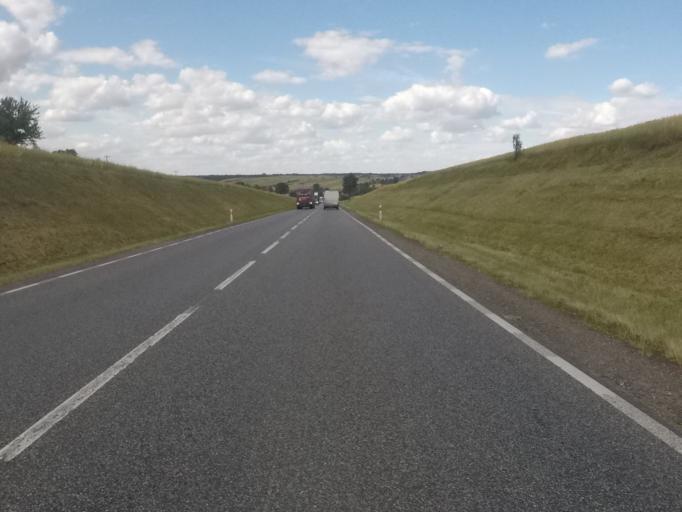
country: PL
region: Lublin Voivodeship
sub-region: Powiat krasnicki
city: Krasnik
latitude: 50.8932
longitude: 22.2652
